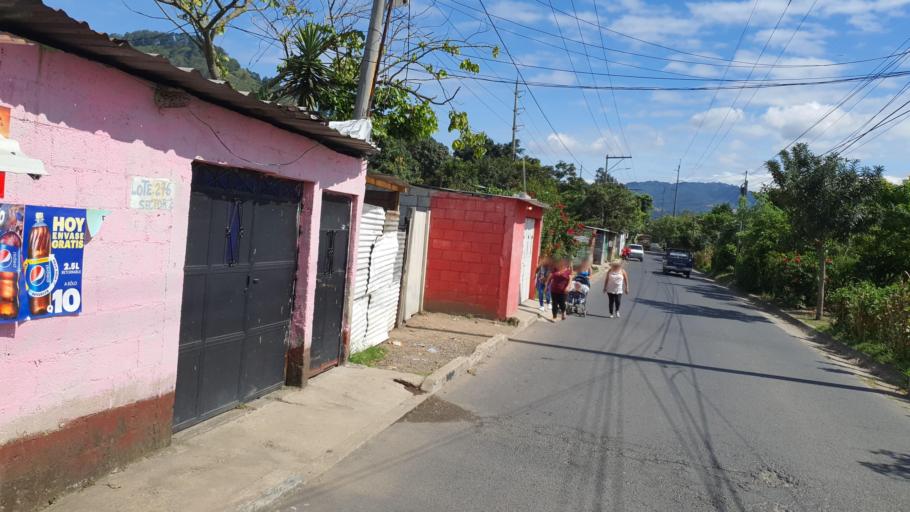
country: GT
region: Guatemala
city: Villa Canales
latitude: 14.4641
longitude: -90.5508
